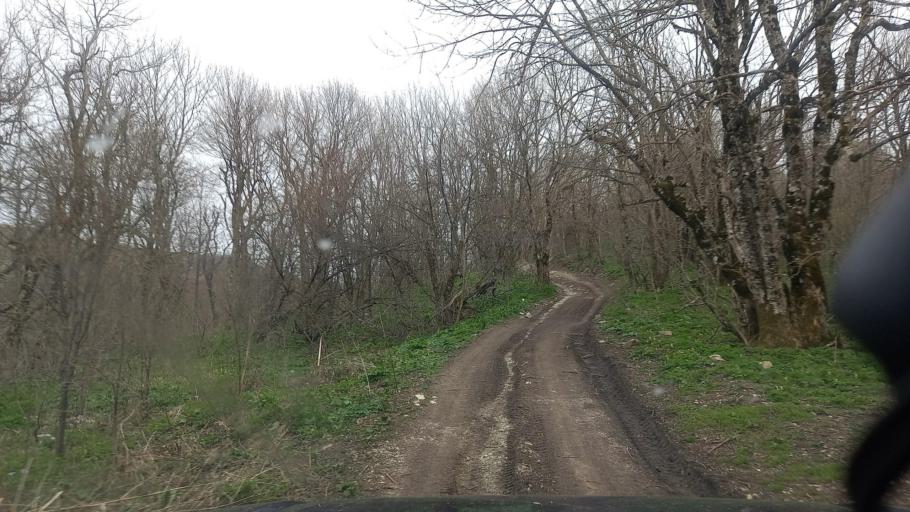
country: RU
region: Krasnodarskiy
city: Gelendzhik
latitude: 44.6148
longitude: 38.2044
